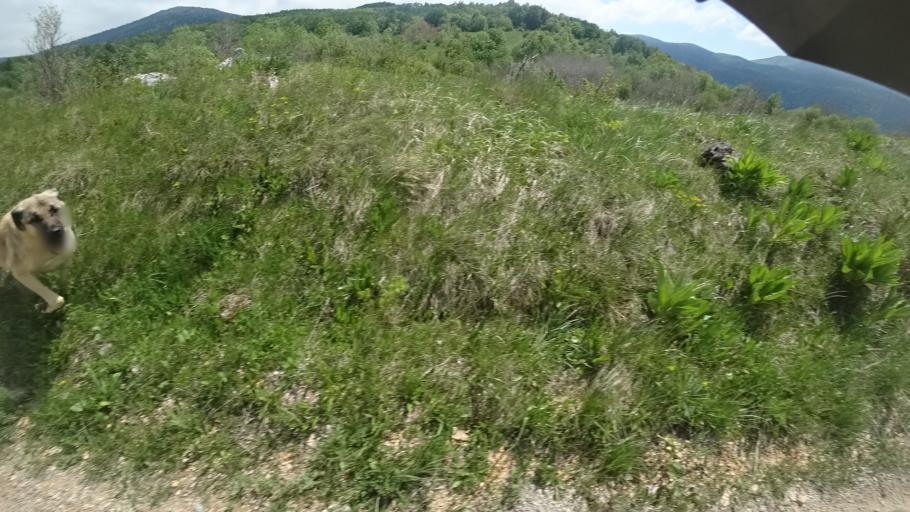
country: HR
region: Zadarska
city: Gracac
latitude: 44.5075
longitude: 15.8867
